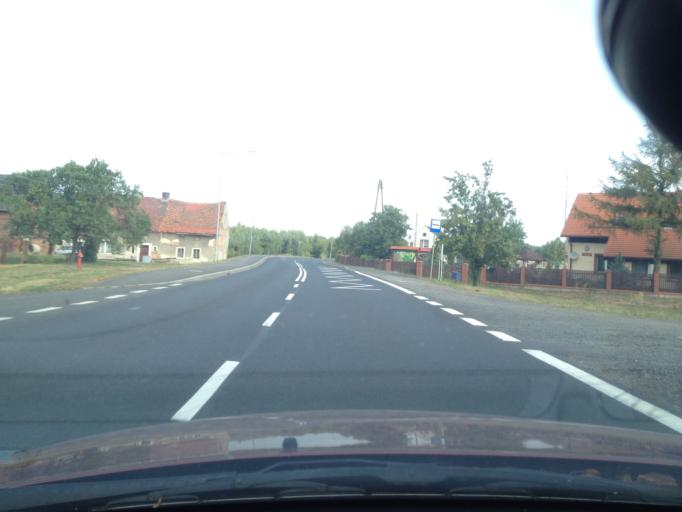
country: PL
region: Lubusz
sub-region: Powiat zaganski
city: Szprotawa
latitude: 51.4366
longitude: 15.6014
